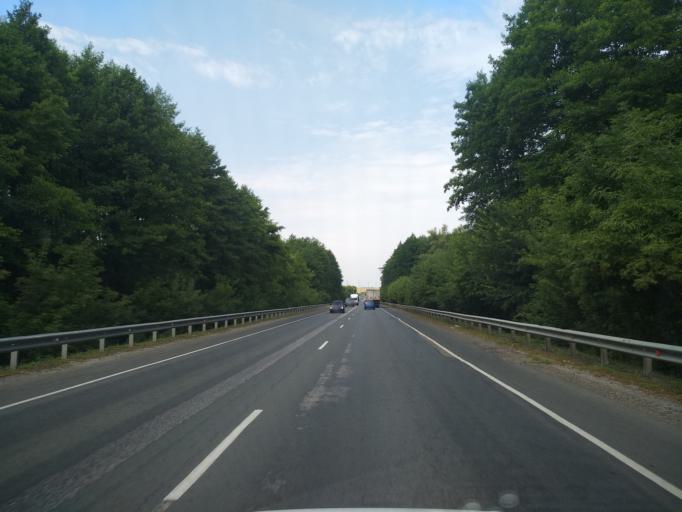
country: RU
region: Voronezj
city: Orlovo
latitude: 51.6815
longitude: 39.5805
